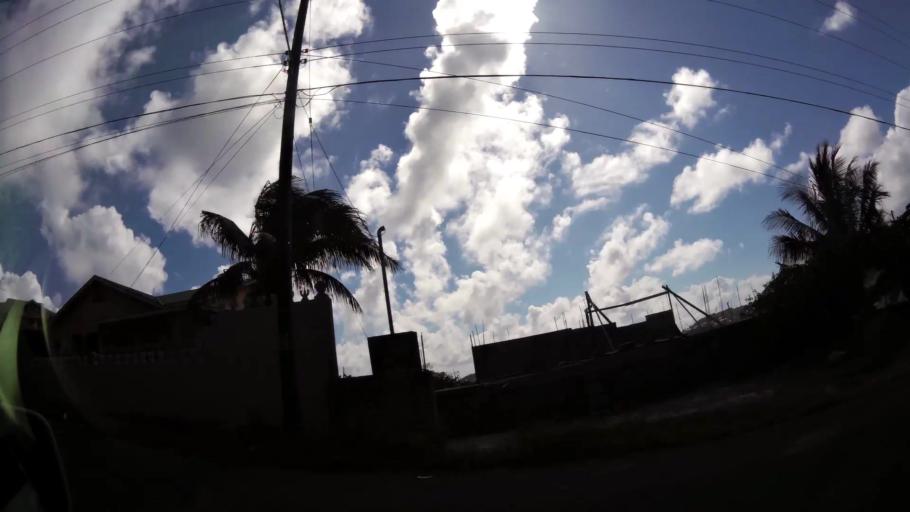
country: VC
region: Saint George
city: Kingstown
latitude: 13.1447
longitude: -61.1648
